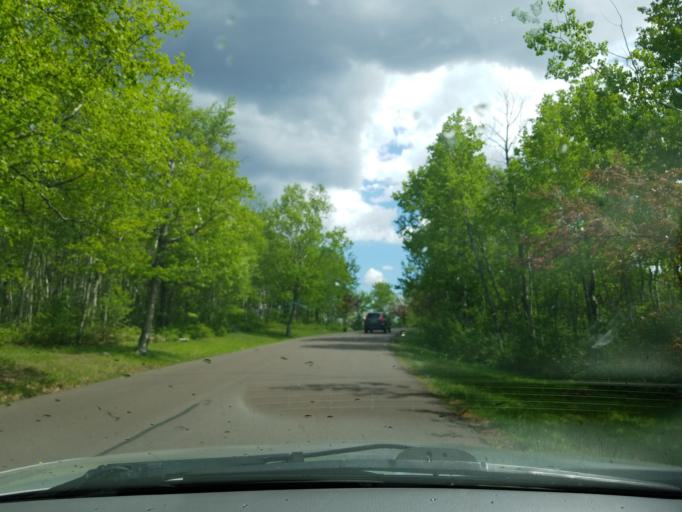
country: US
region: Minnesota
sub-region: Saint Louis County
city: Duluth
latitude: 46.7756
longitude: -92.1266
